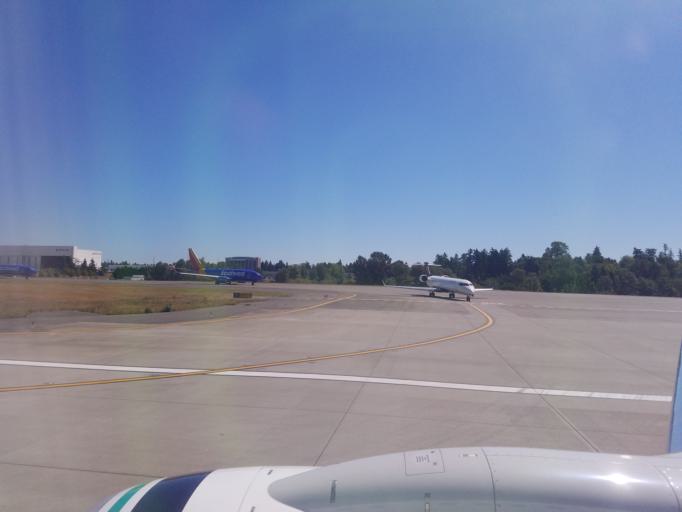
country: US
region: Washington
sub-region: King County
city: SeaTac
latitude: 47.4318
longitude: -122.3080
